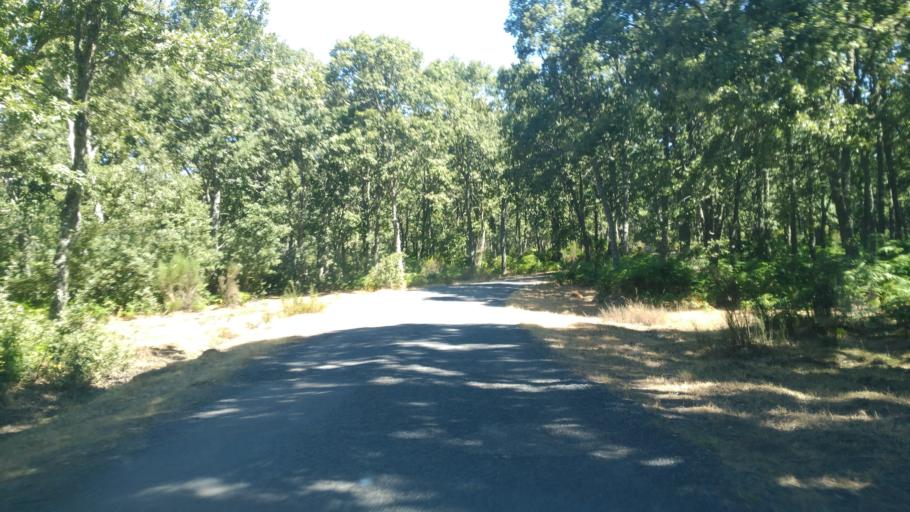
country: ES
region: Castille and Leon
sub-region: Provincia de Salamanca
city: Nava de Francia
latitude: 40.5207
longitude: -6.0998
